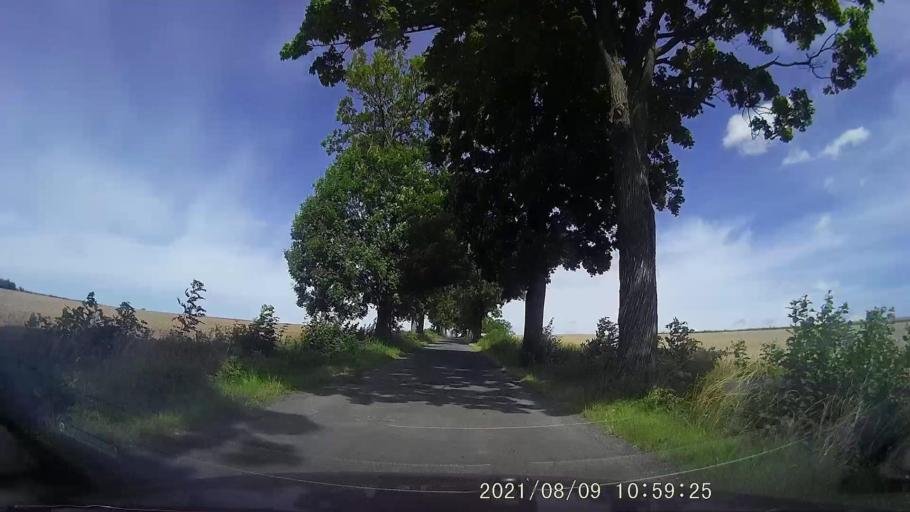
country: PL
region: Lower Silesian Voivodeship
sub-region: Powiat klodzki
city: Polanica-Zdroj
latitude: 50.4491
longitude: 16.5493
